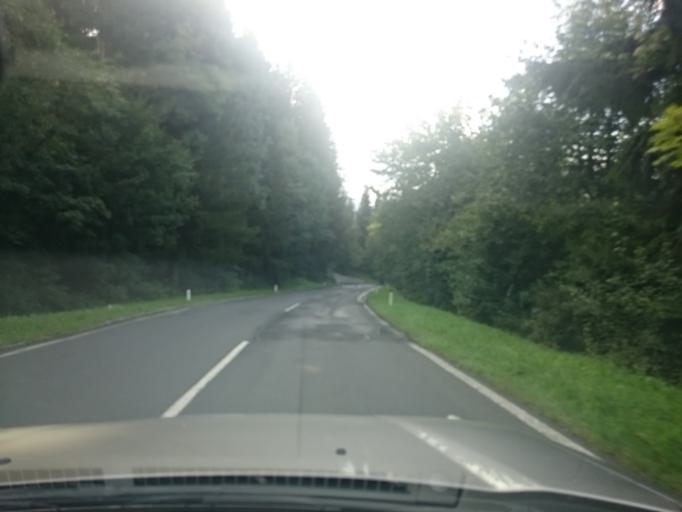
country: AT
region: Carinthia
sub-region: Politischer Bezirk Hermagor
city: Dellach
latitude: 46.6621
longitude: 12.9973
